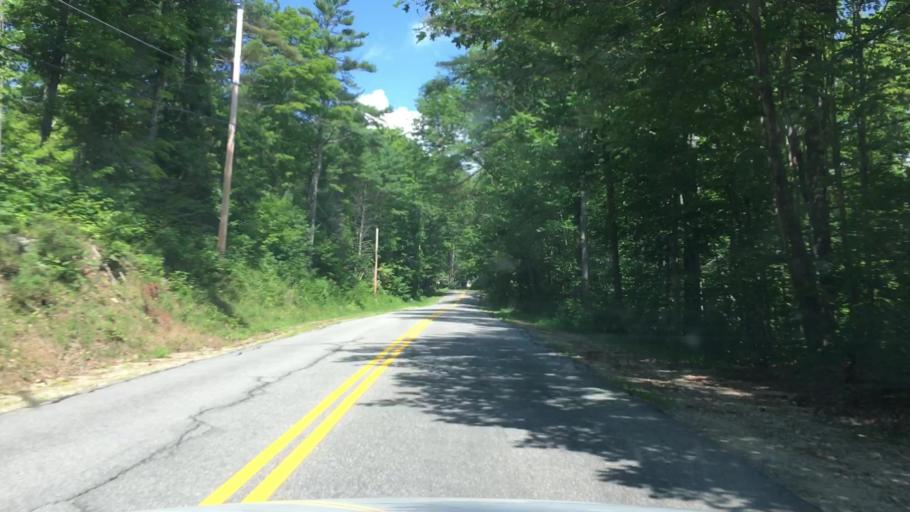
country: US
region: Maine
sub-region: Cumberland County
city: Raymond
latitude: 43.9390
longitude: -70.5225
